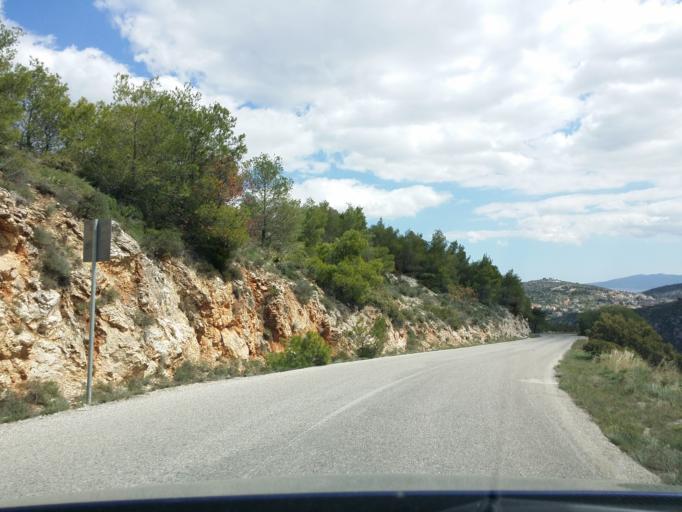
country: GR
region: Attica
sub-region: Nomarchia Dytikis Attikis
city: Fyli
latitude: 38.1171
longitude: 23.6530
